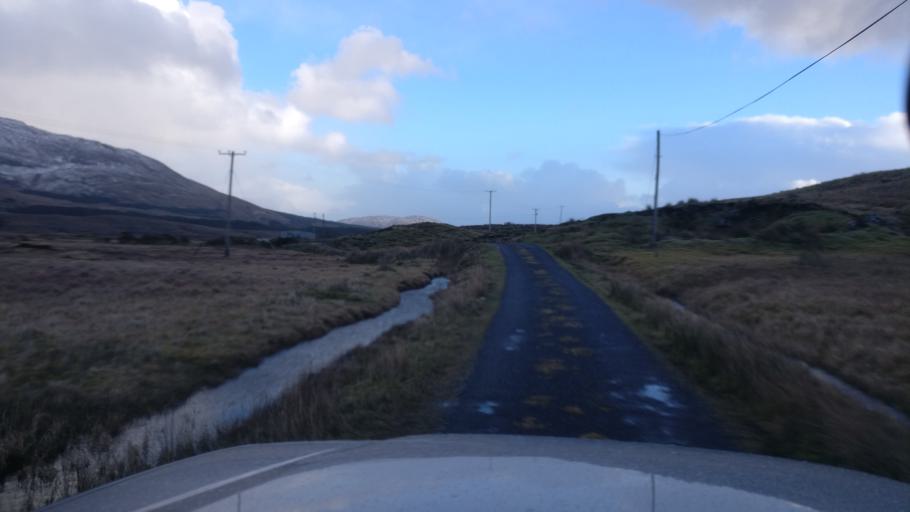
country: IE
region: Connaught
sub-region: County Galway
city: Clifden
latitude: 53.4926
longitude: -9.7028
